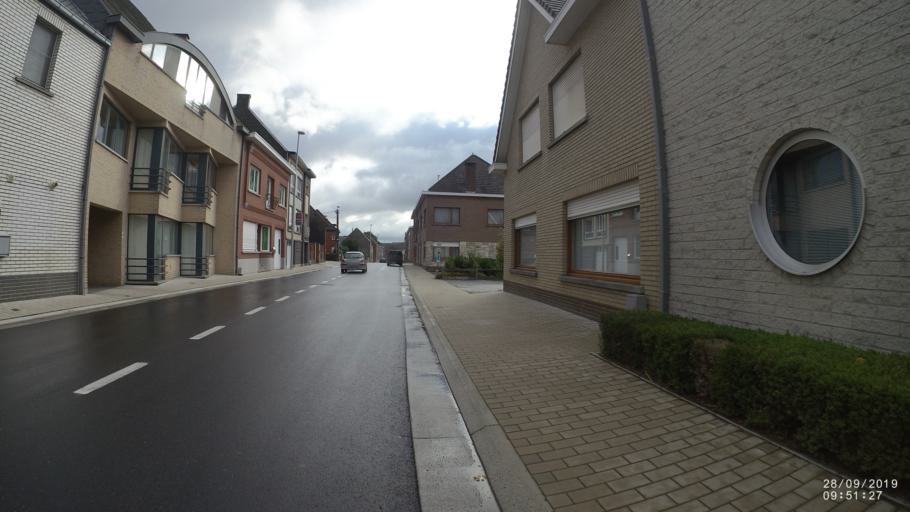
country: BE
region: Wallonia
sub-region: Province du Hainaut
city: Flobecq
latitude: 50.8057
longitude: 3.7584
